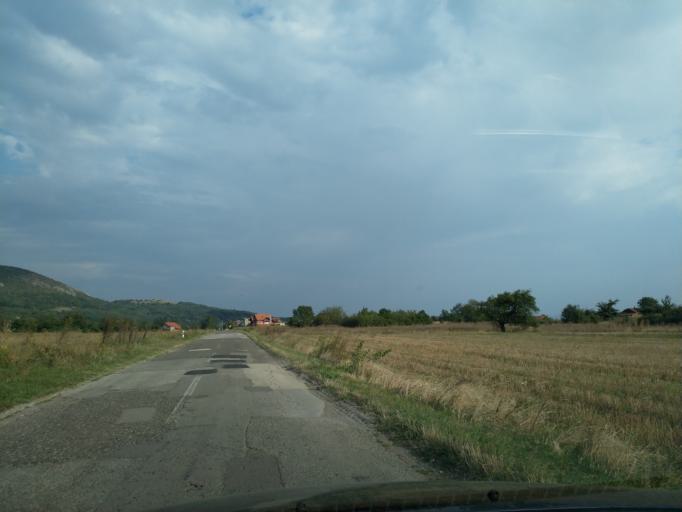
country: RS
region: Central Serbia
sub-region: Pomoravski Okrug
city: Paracin
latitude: 43.8236
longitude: 21.5330
